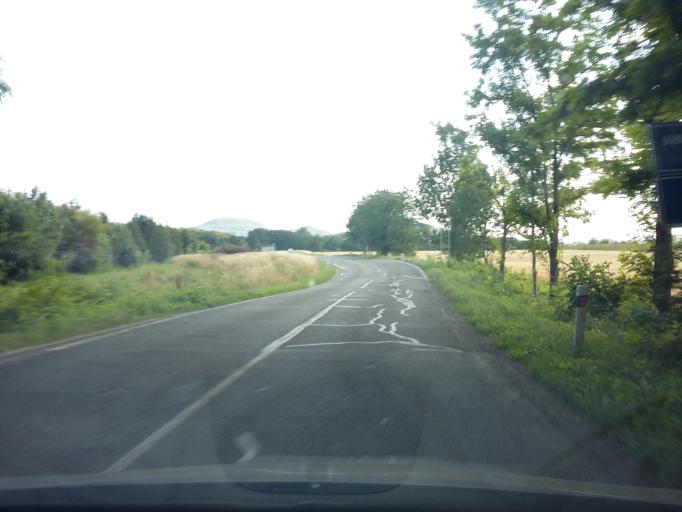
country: SK
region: Trnavsky
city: Smolenice
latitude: 48.5227
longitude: 17.3137
